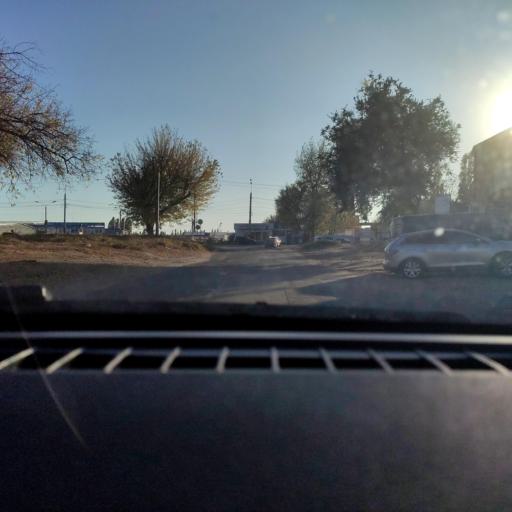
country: RU
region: Voronezj
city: Voronezh
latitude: 51.6585
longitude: 39.2857
